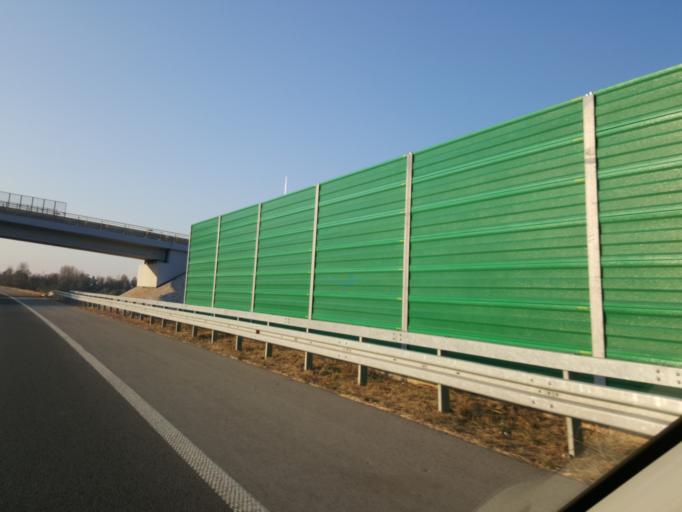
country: RS
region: Central Serbia
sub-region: Pirotski Okrug
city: Dimitrovgrad
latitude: 43.0588
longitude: 22.6914
